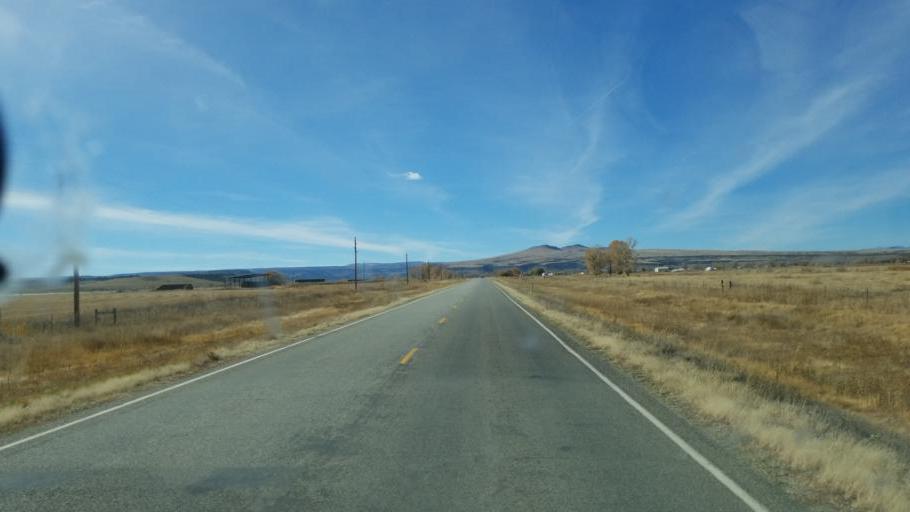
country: US
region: Colorado
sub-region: Conejos County
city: Conejos
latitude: 37.0645
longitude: -106.0420
